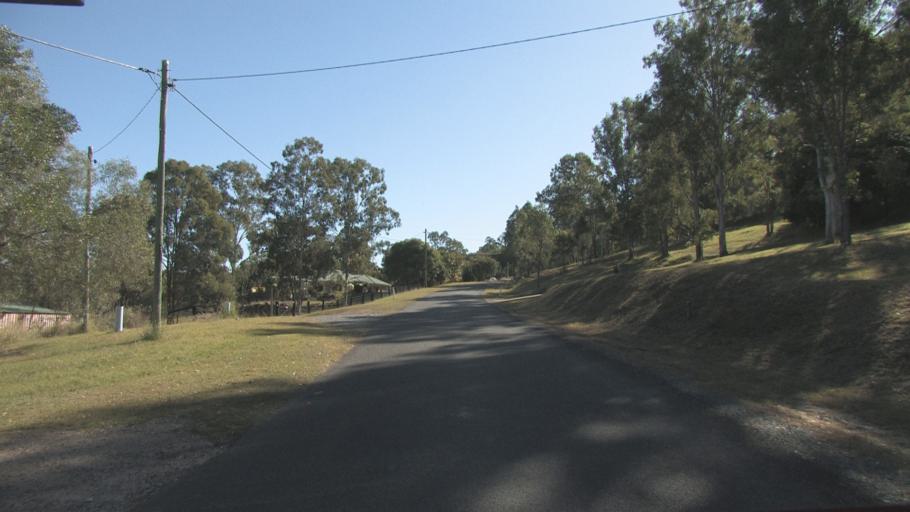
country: AU
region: Queensland
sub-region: Logan
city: Windaroo
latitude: -27.7798
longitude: 153.1481
